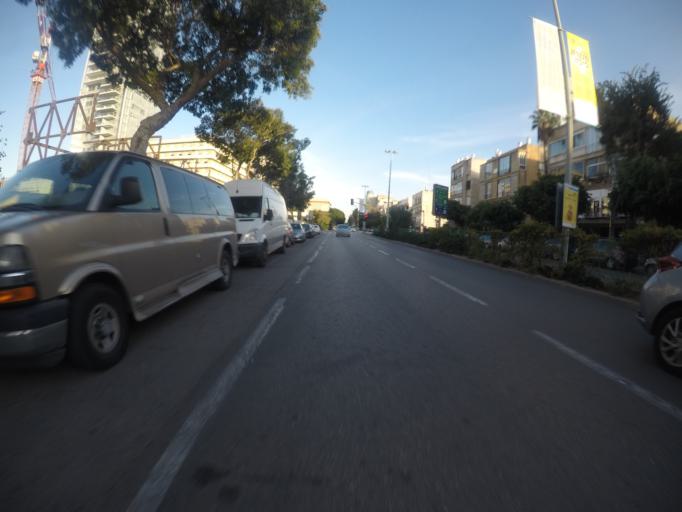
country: IL
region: Tel Aviv
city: Tel Aviv
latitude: 32.0847
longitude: 34.7850
